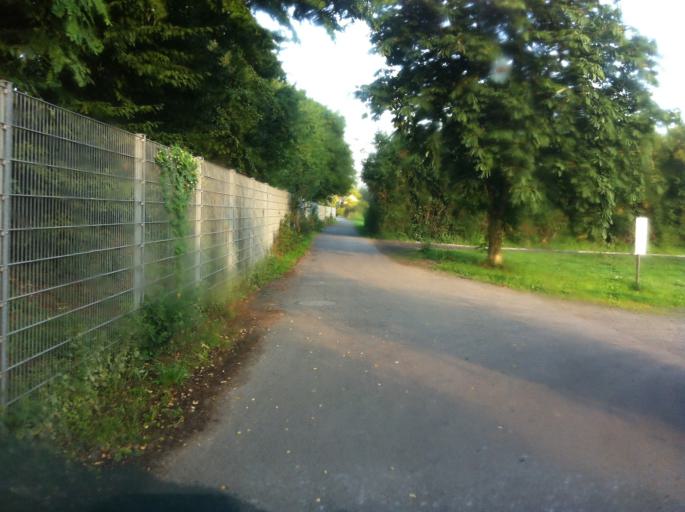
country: DE
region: Rheinland-Pfalz
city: Erpel
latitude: 50.5766
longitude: 7.2476
